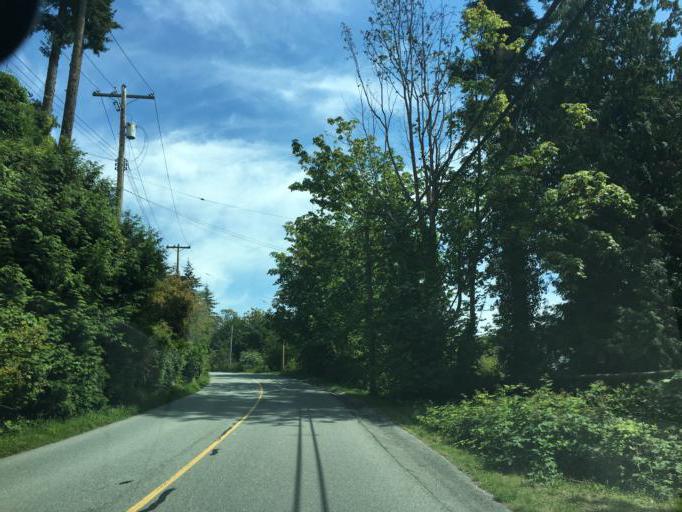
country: CA
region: British Columbia
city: West Vancouver
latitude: 49.3415
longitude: -123.2333
